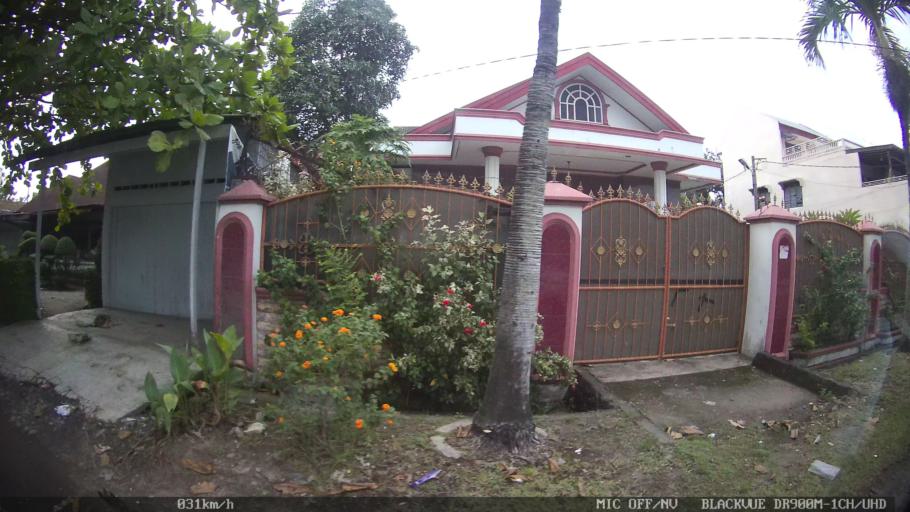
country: ID
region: North Sumatra
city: Medan
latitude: 3.6071
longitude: 98.7006
